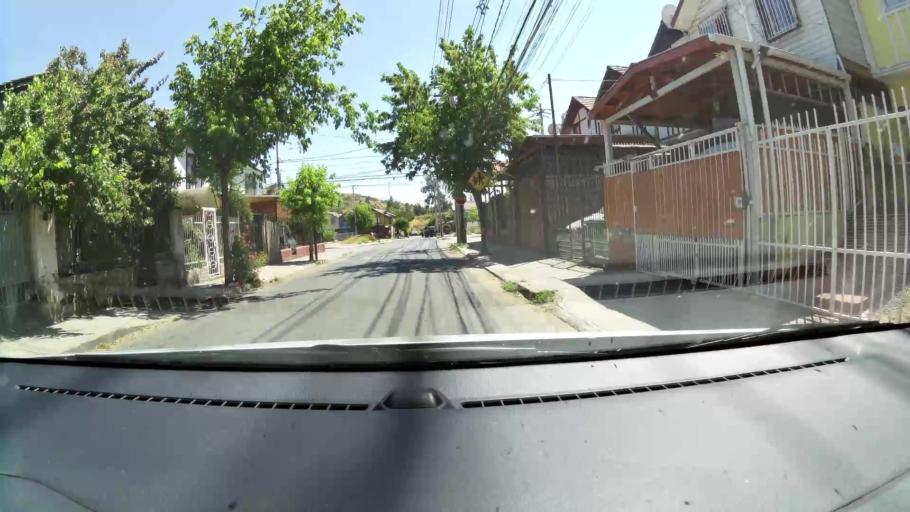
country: CL
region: Santiago Metropolitan
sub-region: Provincia de Maipo
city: San Bernardo
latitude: -33.6265
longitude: -70.7056
